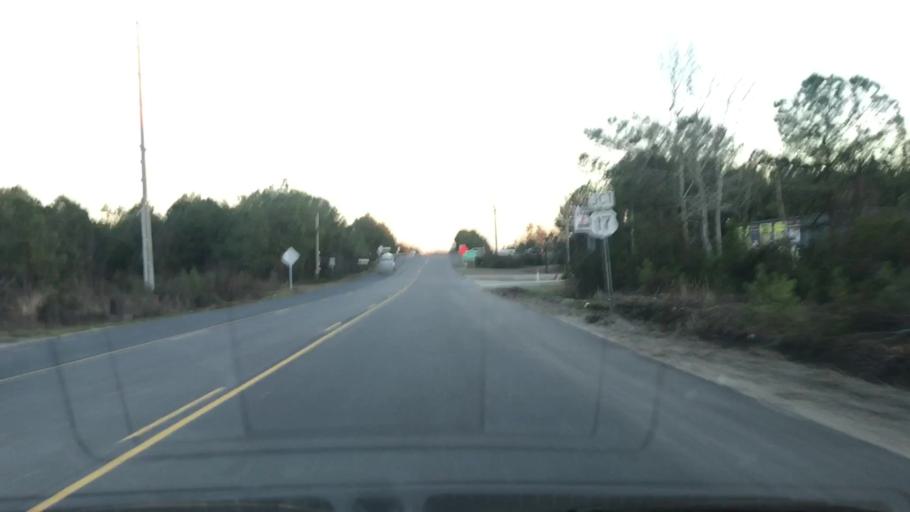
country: US
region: North Carolina
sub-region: Brunswick County
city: Shallotte
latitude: 33.9781
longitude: -78.4087
